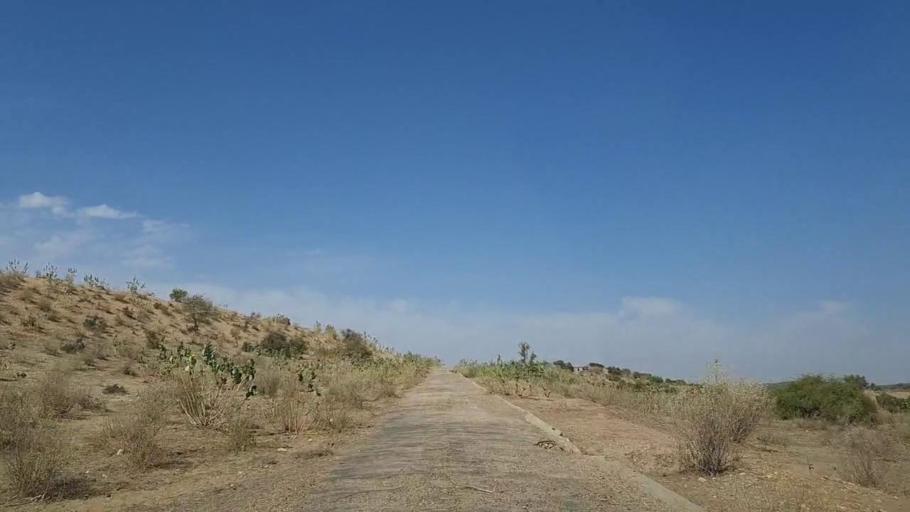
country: PK
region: Sindh
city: Nabisar
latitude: 24.8786
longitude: 69.6124
